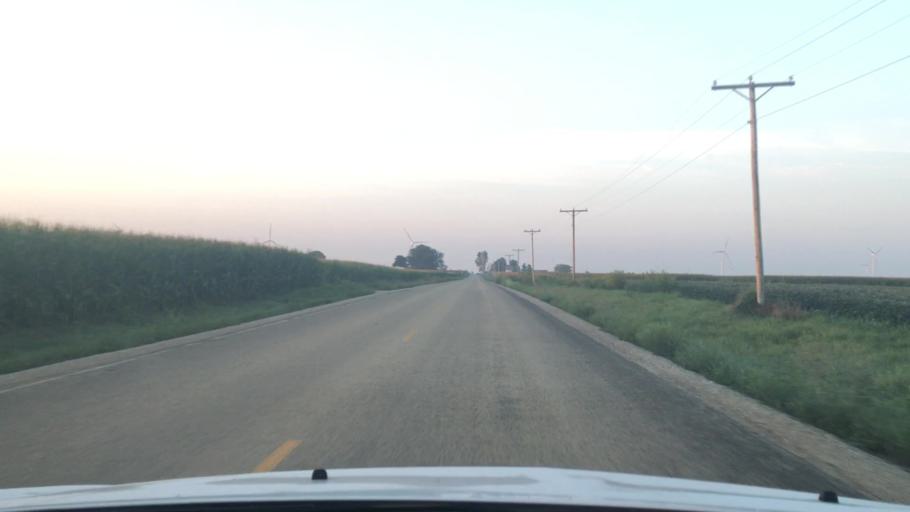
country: US
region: Illinois
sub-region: DeKalb County
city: Waterman
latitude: 41.8430
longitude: -88.7734
